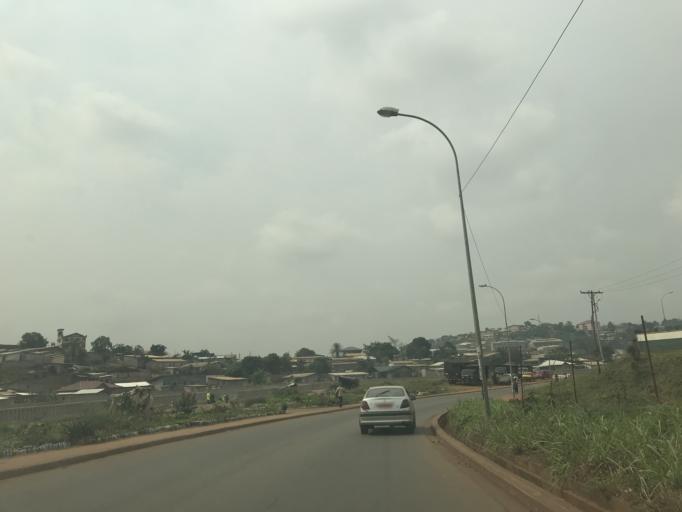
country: CM
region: Centre
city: Yaounde
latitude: 3.8311
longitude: 11.5154
